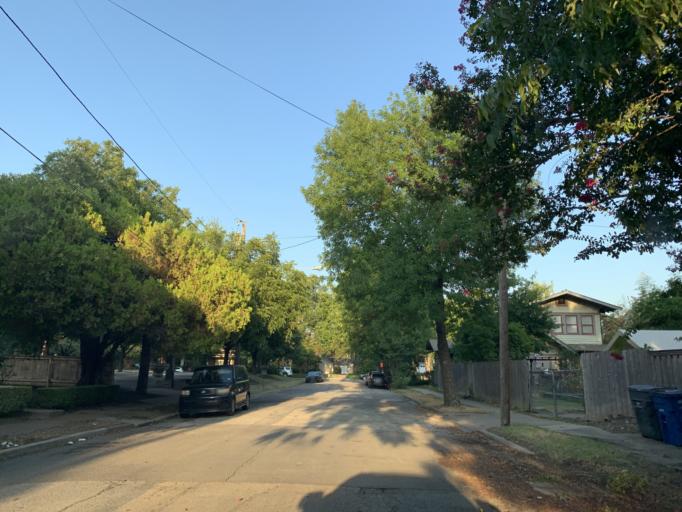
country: US
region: Texas
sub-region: Dallas County
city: Cockrell Hill
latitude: 32.7477
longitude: -96.8488
